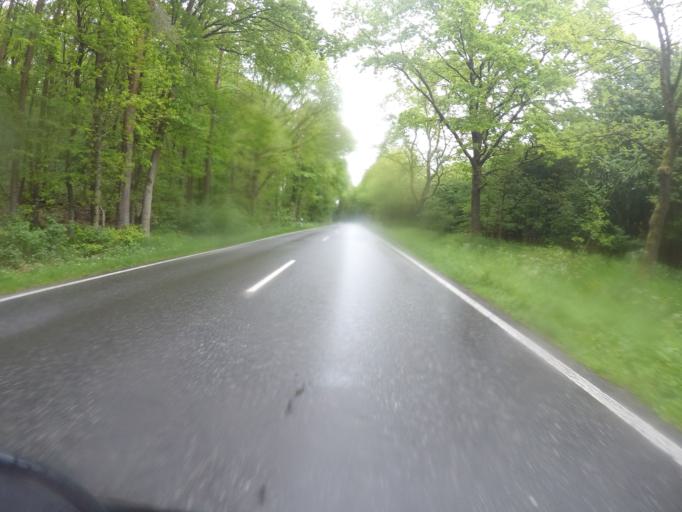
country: DE
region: Schleswig-Holstein
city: Heidmuhlen
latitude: 53.9485
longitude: 10.0852
